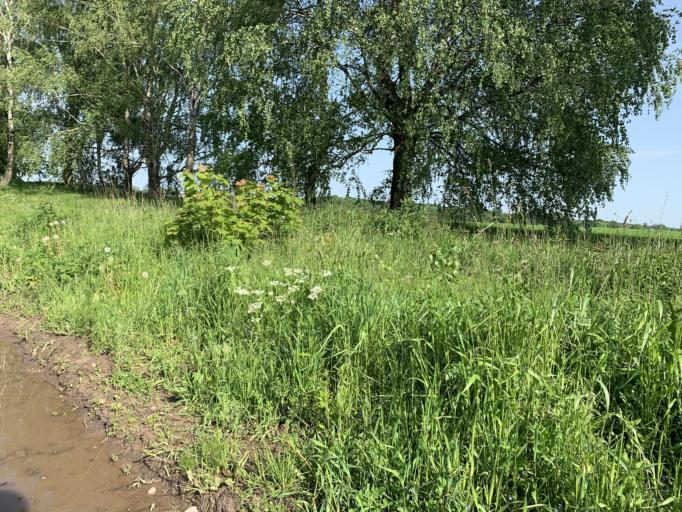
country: BY
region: Minsk
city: Kapyl'
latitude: 53.2635
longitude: 26.9399
